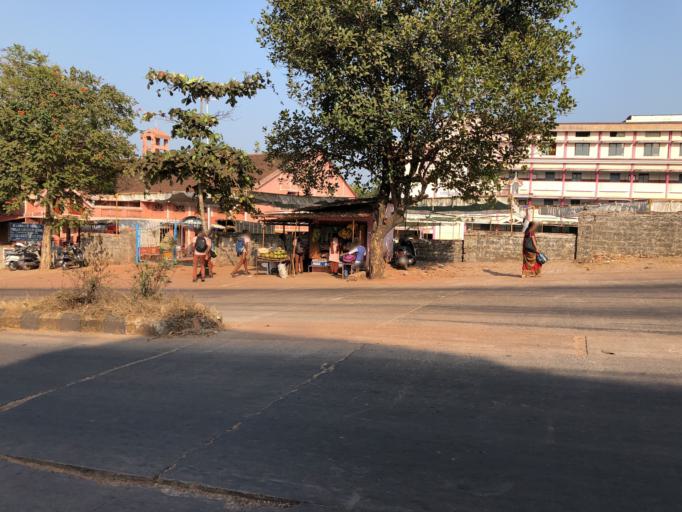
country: IN
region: Karnataka
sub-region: Dakshina Kannada
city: Mangalore
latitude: 12.9167
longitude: 74.8685
